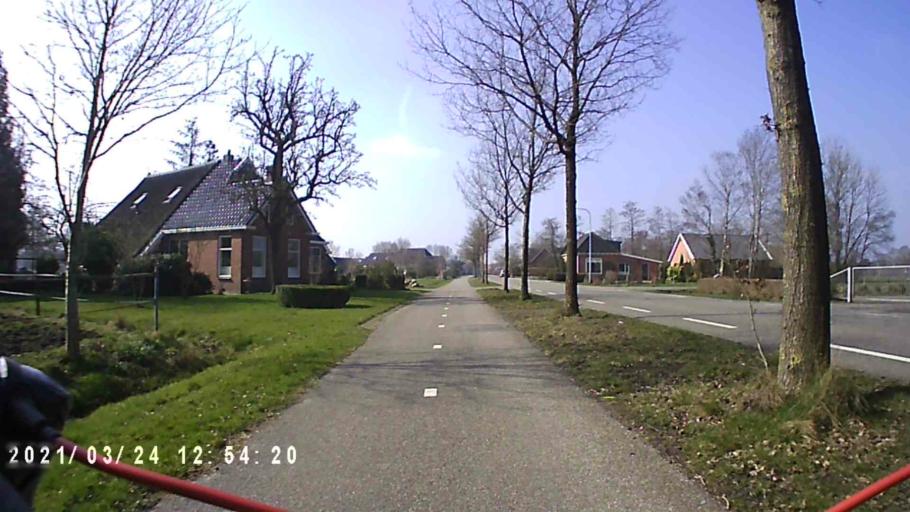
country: NL
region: Groningen
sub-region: Gemeente Leek
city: Leek
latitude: 53.1547
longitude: 6.3158
